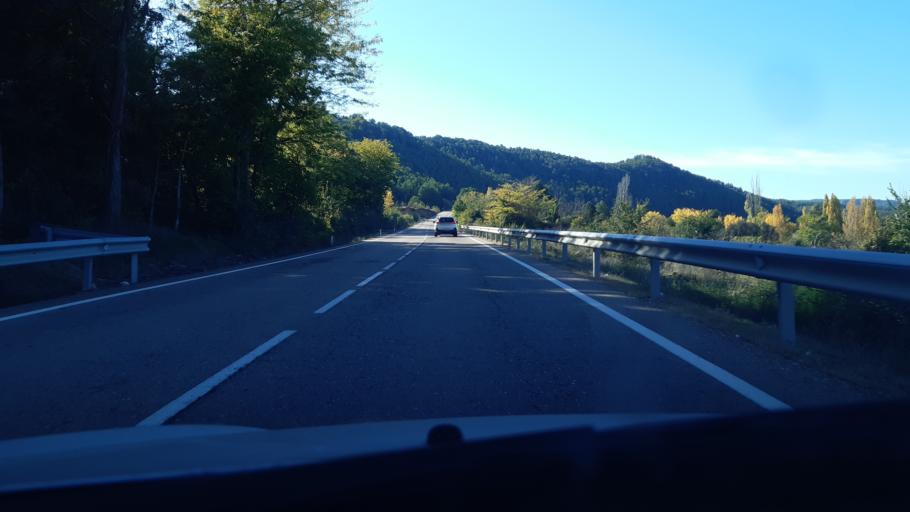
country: ES
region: Aragon
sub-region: Provincia de Teruel
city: Valderrobres
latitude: 40.8829
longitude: 0.1263
